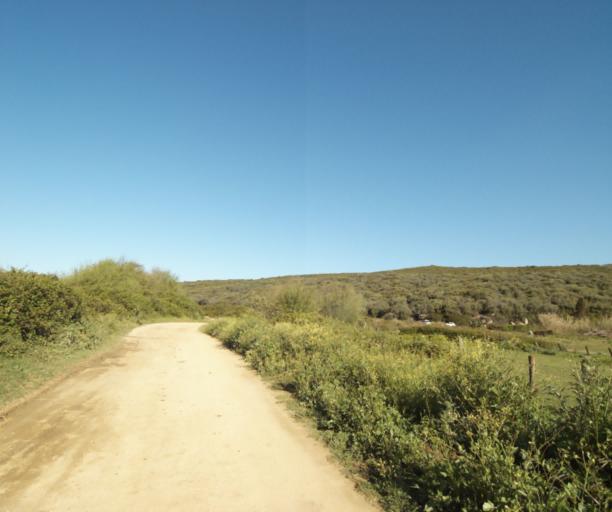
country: FR
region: Corsica
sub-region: Departement de la Corse-du-Sud
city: Propriano
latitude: 41.6638
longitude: 8.8934
